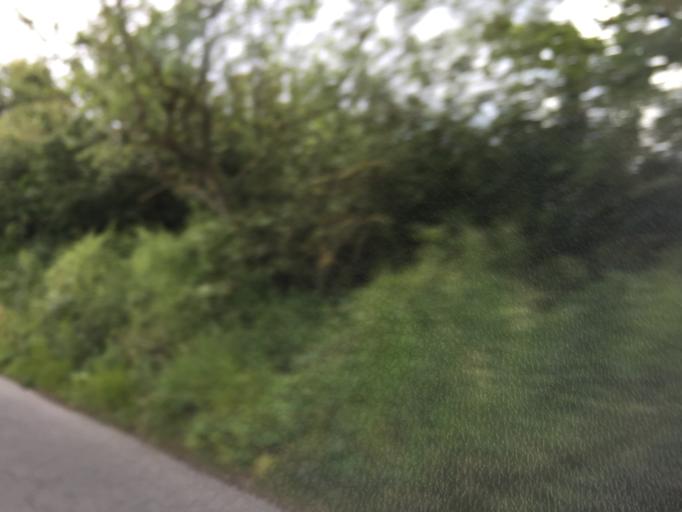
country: GB
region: England
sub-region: Wiltshire
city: Purton
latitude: 51.6088
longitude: -1.8491
